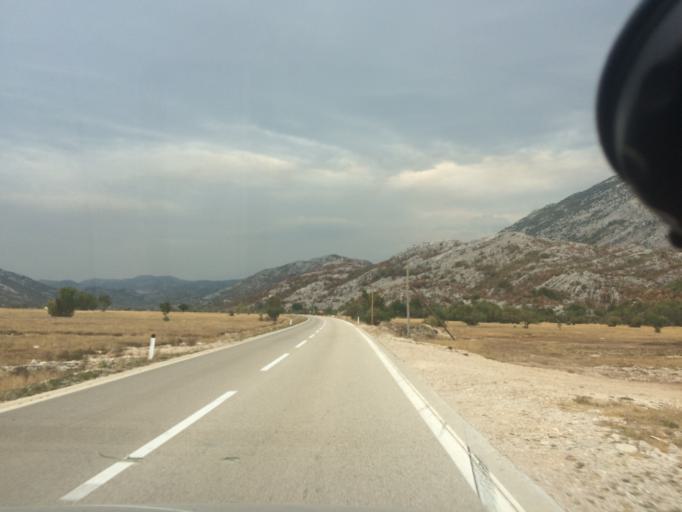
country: ME
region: Kotor
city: Risan
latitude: 42.5961
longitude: 18.6903
